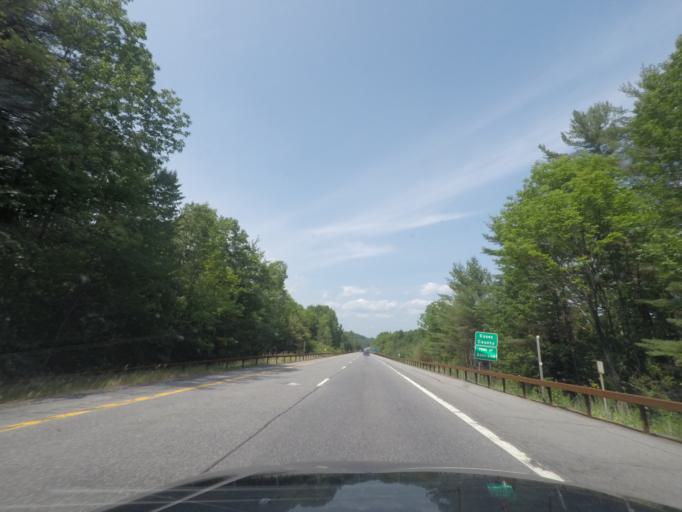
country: US
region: New York
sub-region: Warren County
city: Warrensburg
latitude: 43.7690
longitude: -73.8021
